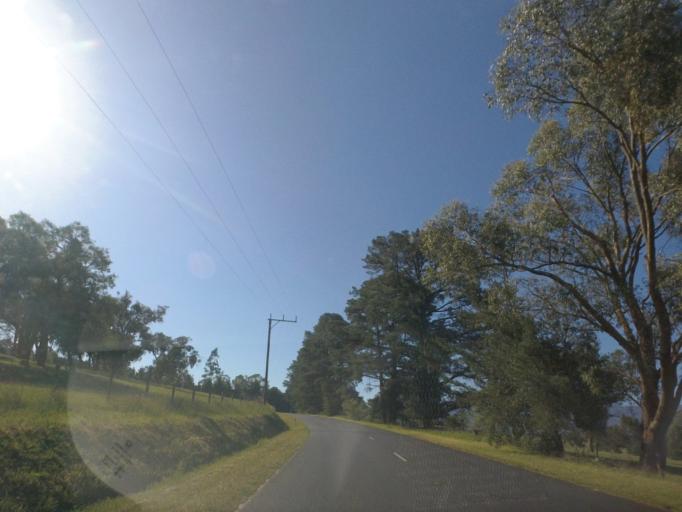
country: AU
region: Victoria
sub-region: Yarra Ranges
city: Yarra Junction
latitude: -37.8079
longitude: 145.6384
